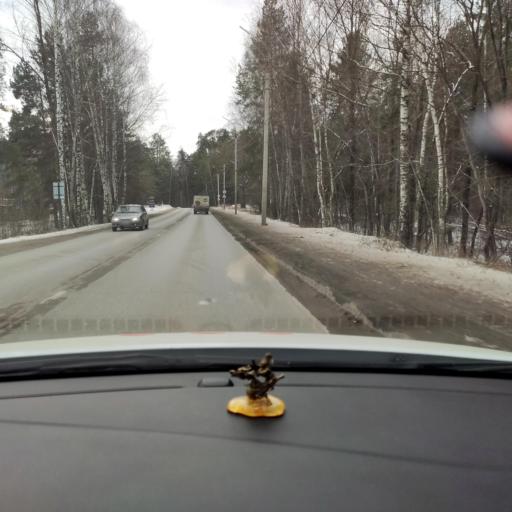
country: RU
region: Tatarstan
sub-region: Zelenodol'skiy Rayon
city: Zelenodolsk
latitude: 55.8646
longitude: 48.5367
